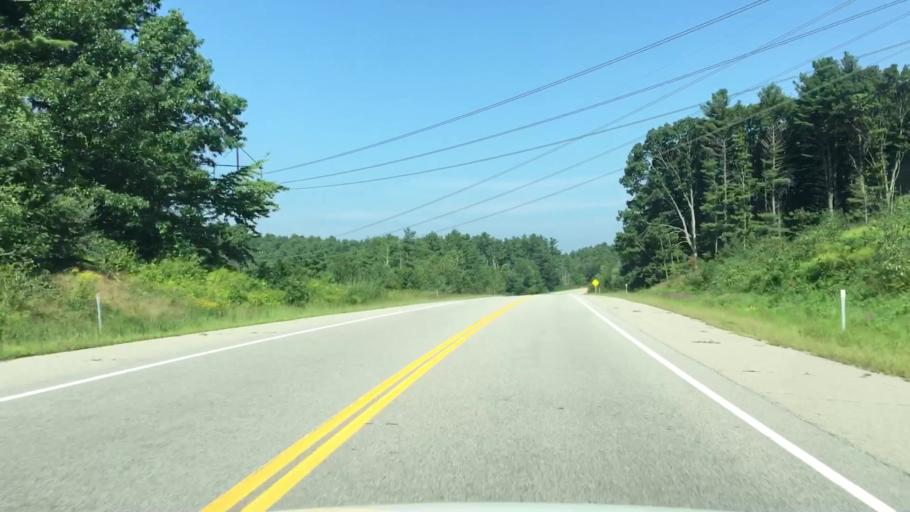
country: US
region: New Hampshire
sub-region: Rockingham County
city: Seabrook
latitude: 42.8996
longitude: -70.9061
